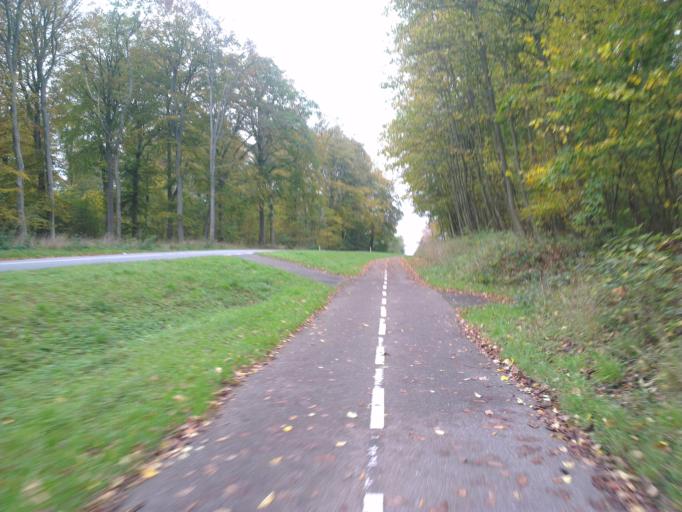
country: DK
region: Capital Region
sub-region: Frederikssund Kommune
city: Frederikssund
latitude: 55.8502
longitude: 12.0249
